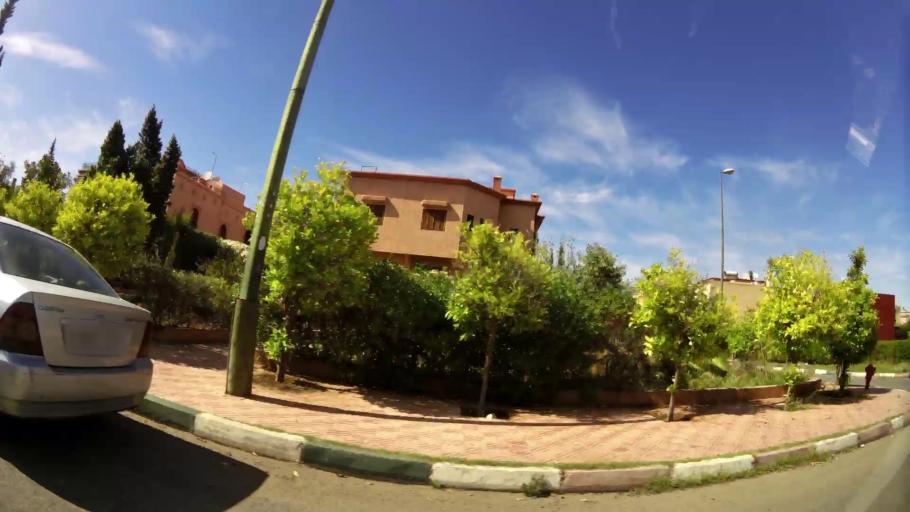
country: MA
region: Marrakech-Tensift-Al Haouz
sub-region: Marrakech
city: Marrakesh
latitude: 31.6545
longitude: -8.0556
